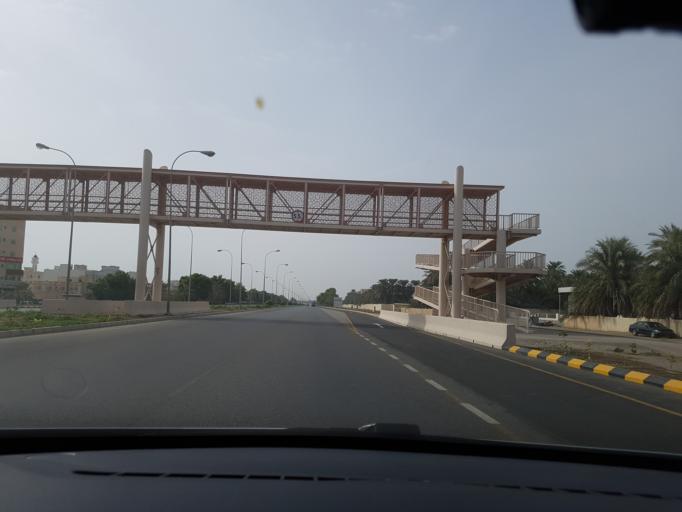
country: OM
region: Al Batinah
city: Al Sohar
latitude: 24.3600
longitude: 56.7100
